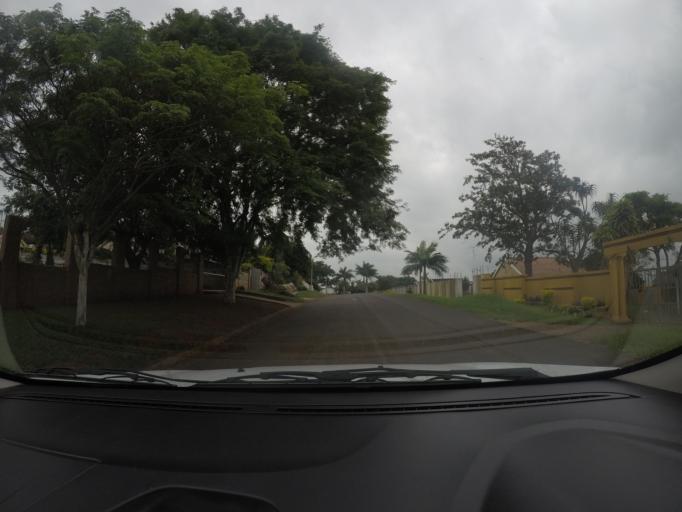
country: ZA
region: KwaZulu-Natal
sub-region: uThungulu District Municipality
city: Empangeni
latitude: -28.7366
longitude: 31.9007
